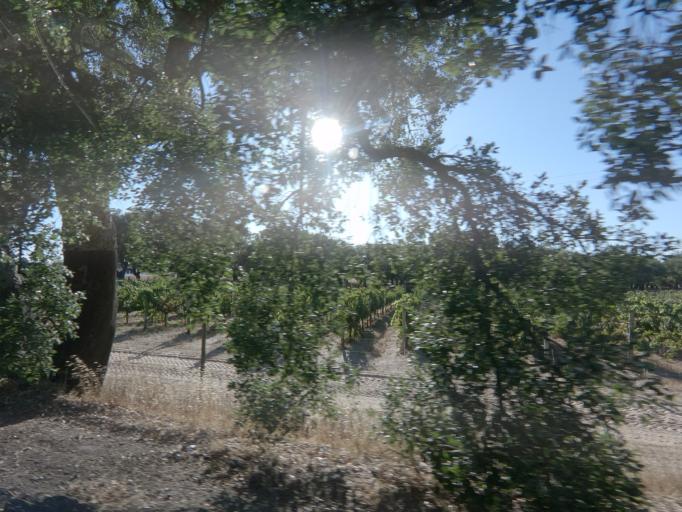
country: PT
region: Setubal
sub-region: Palmela
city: Quinta do Anjo
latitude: 38.5417
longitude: -8.9855
